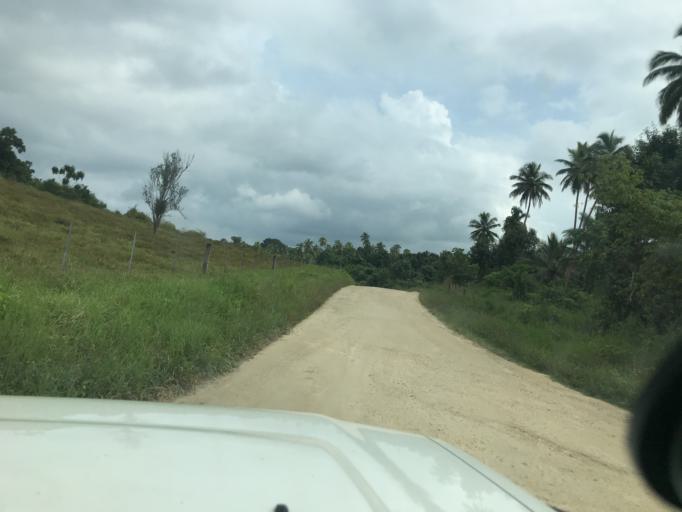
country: VU
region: Sanma
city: Luganville
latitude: -15.5809
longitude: 167.0244
